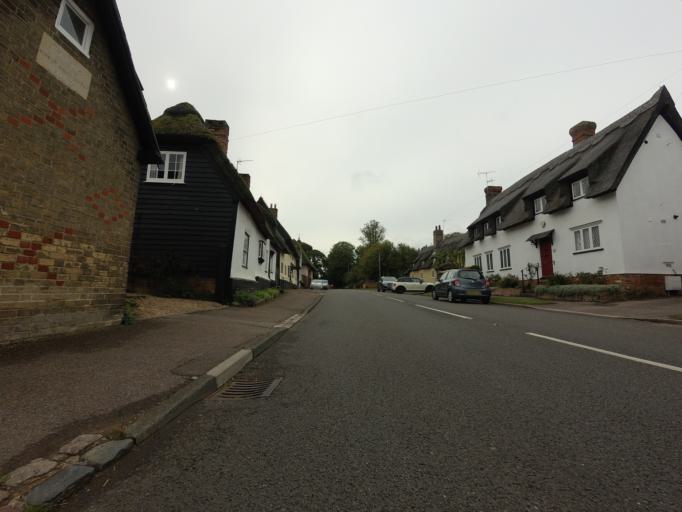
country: GB
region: England
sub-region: Hertfordshire
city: Reed
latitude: 51.9994
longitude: 0.0144
